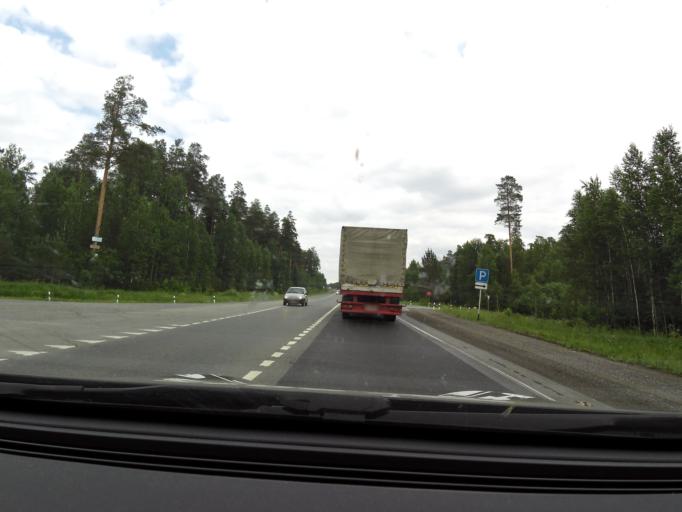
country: RU
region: Sverdlovsk
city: Druzhinino
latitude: 56.8380
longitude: 59.6533
